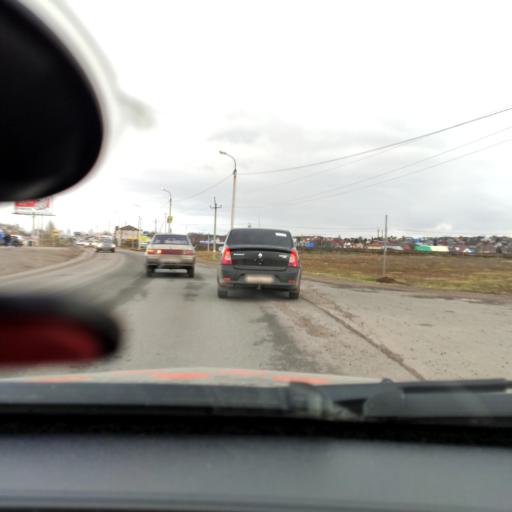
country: RU
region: Bashkortostan
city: Kabakovo
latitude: 54.6435
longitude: 56.0822
